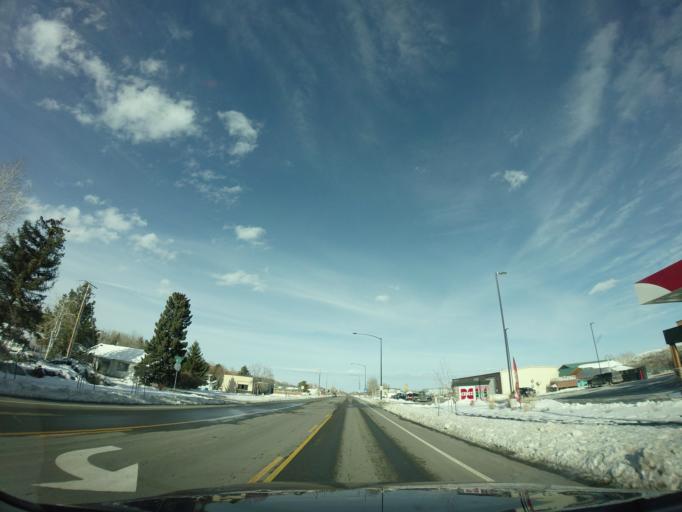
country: US
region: Montana
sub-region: Carbon County
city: Red Lodge
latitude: 45.1963
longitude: -109.2467
